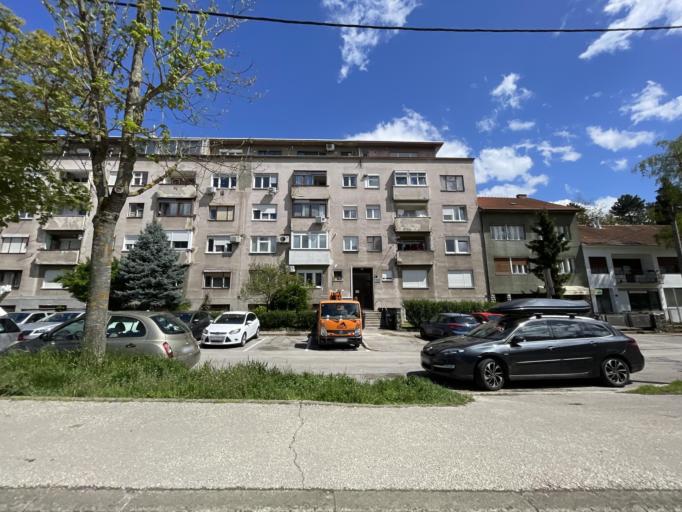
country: HR
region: Grad Zagreb
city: Zagreb - Centar
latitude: 45.8164
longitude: 15.9449
